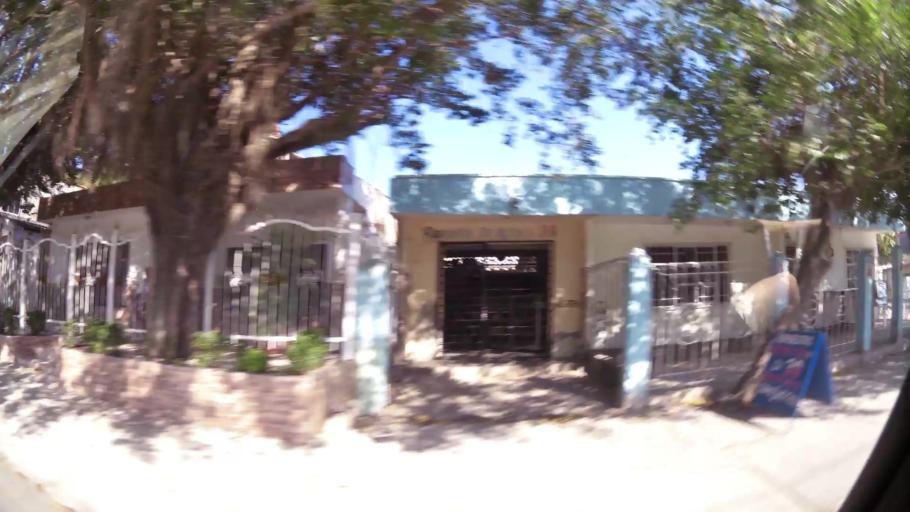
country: CO
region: Bolivar
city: Cartagena
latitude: 10.4238
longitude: -75.5200
